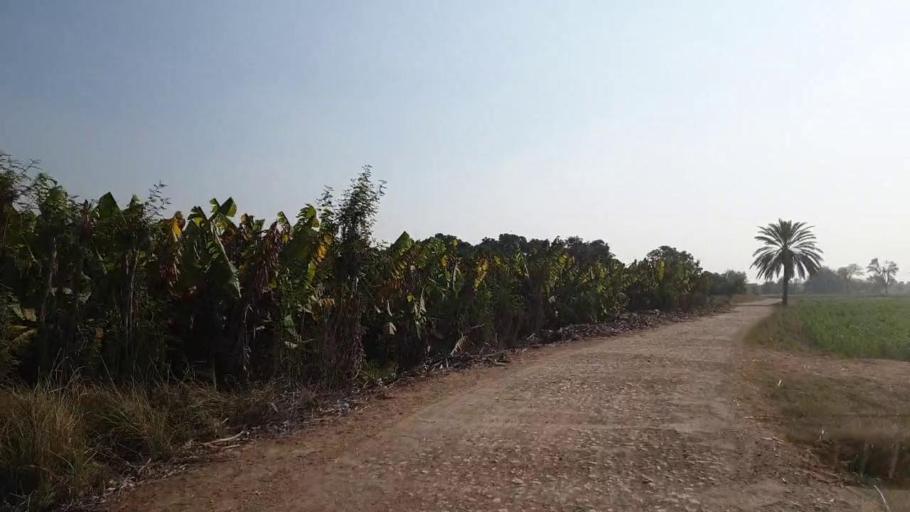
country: PK
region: Sindh
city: Tando Adam
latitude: 25.6806
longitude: 68.5663
